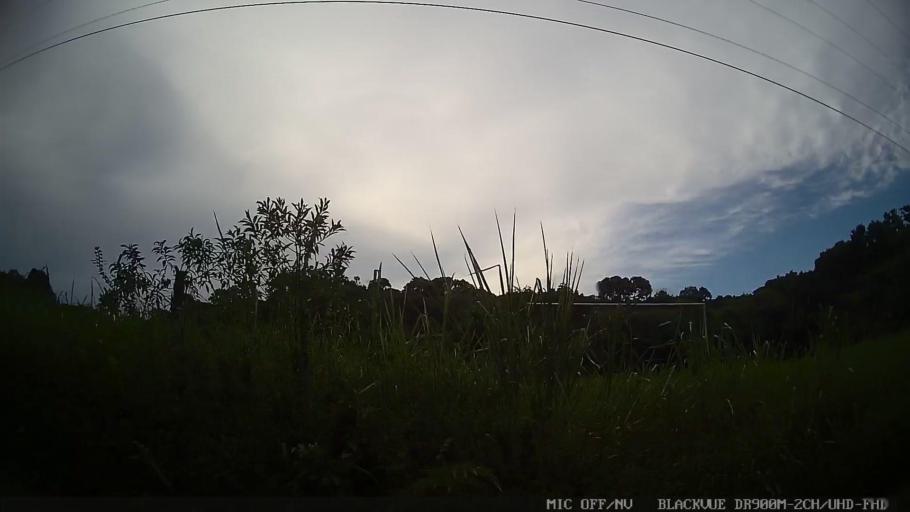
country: BR
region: Sao Paulo
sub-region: Iguape
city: Iguape
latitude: -24.6684
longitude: -47.4403
